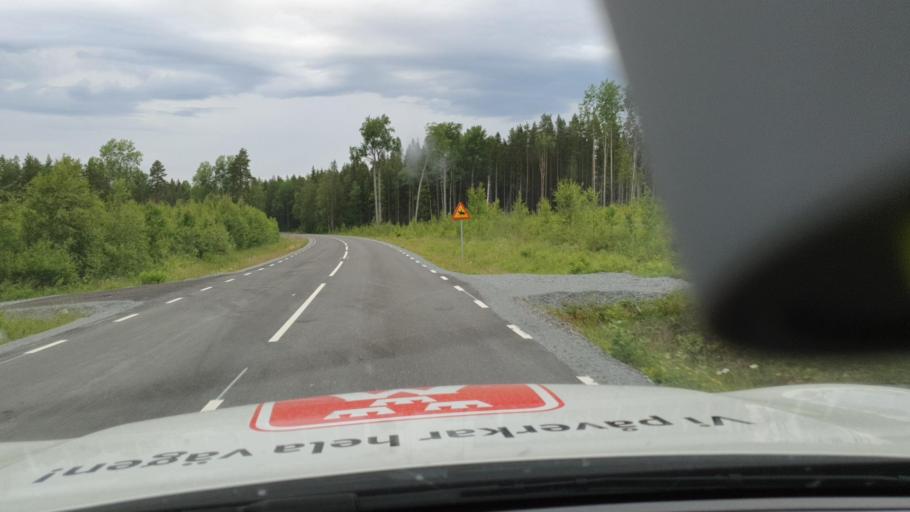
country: SE
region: OErebro
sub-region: Laxa Kommun
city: Laxa
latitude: 58.8593
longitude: 14.5449
